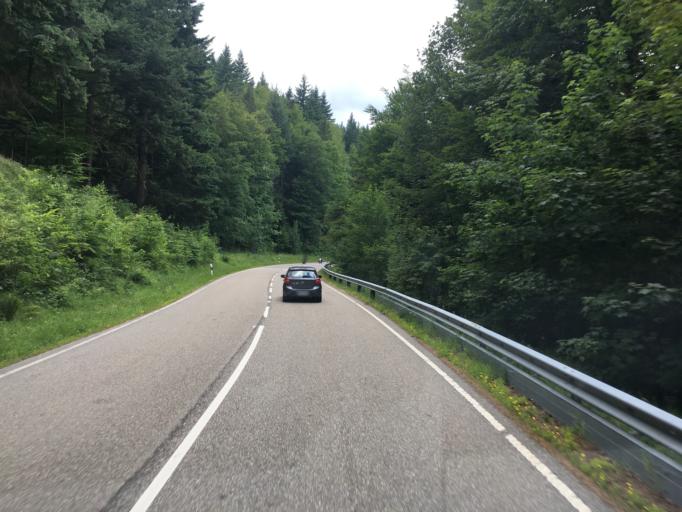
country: DE
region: Baden-Wuerttemberg
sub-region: Karlsruhe Region
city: Buhlertal
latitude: 48.6925
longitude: 8.2342
